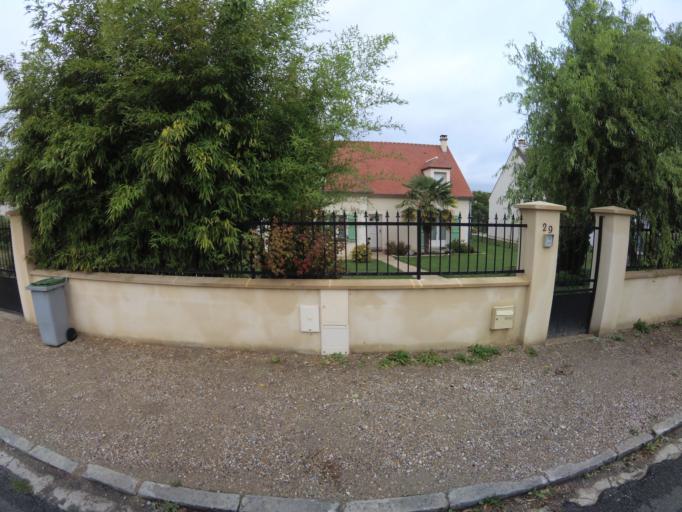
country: FR
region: Ile-de-France
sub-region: Departement de Seine-et-Marne
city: Guermantes
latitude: 48.8550
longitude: 2.7026
